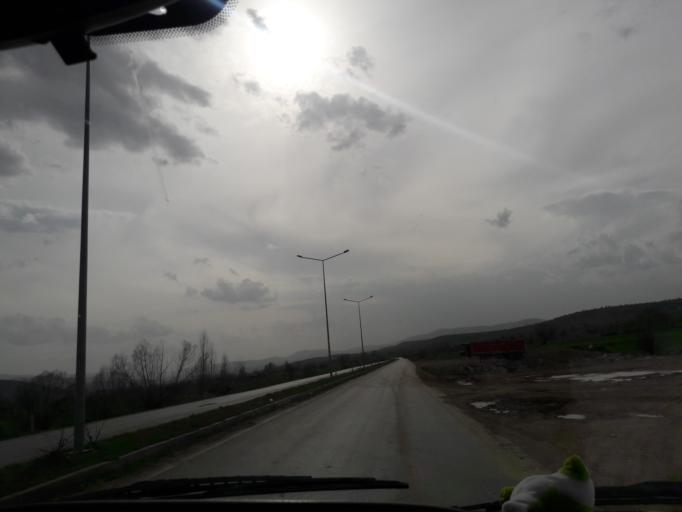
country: TR
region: Gumushane
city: Siran
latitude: 40.1772
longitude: 39.1057
